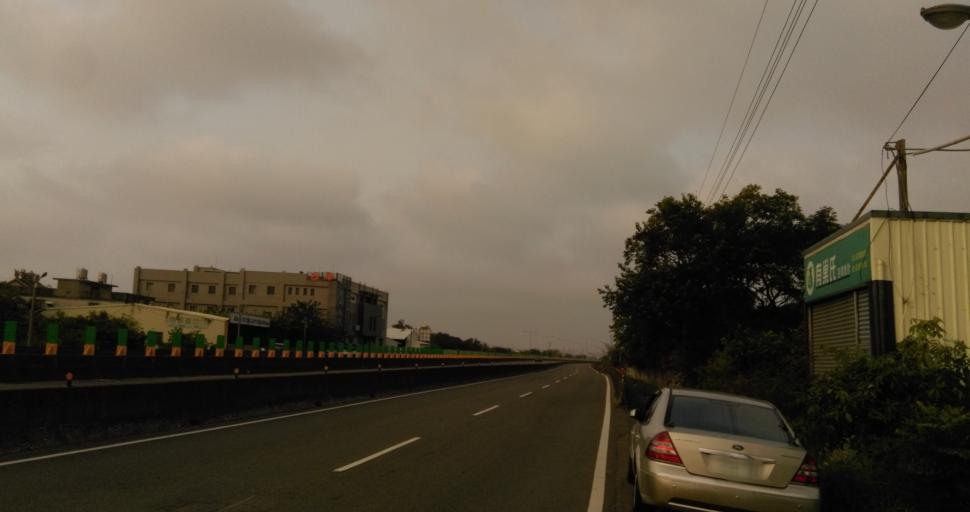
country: TW
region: Taiwan
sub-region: Hsinchu
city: Hsinchu
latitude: 24.7878
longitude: 120.9176
